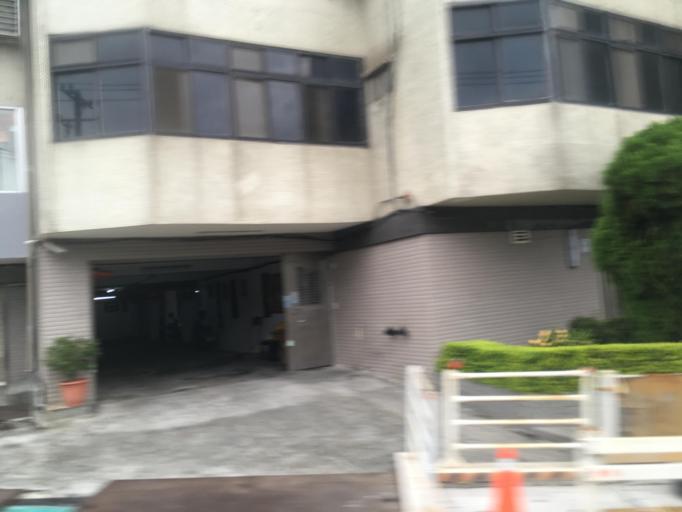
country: TW
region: Taipei
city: Taipei
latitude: 25.1288
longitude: 121.5287
